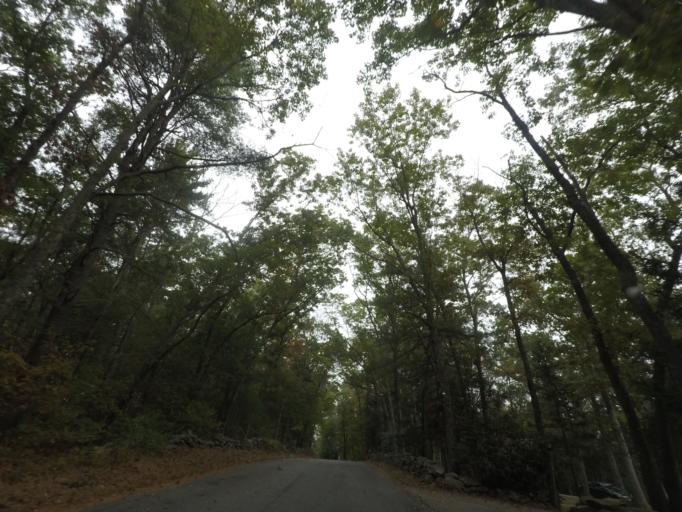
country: US
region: Connecticut
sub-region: Windham County
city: Thompson
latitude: 41.9649
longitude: -71.8333
